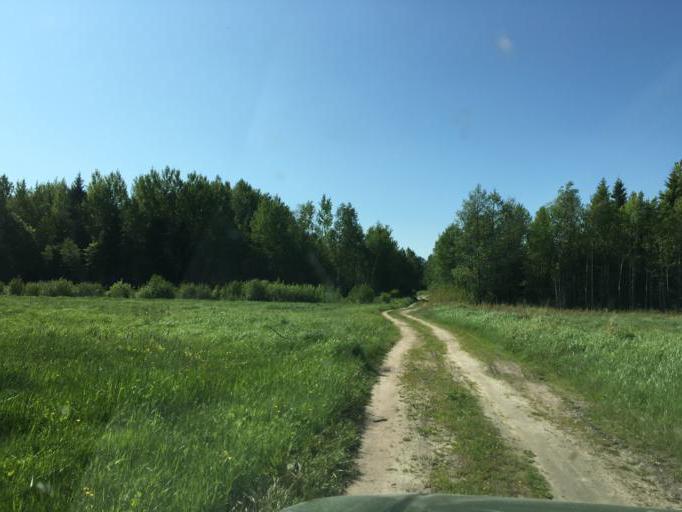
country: LV
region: Ventspils
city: Ventspils
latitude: 57.4801
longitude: 21.7630
